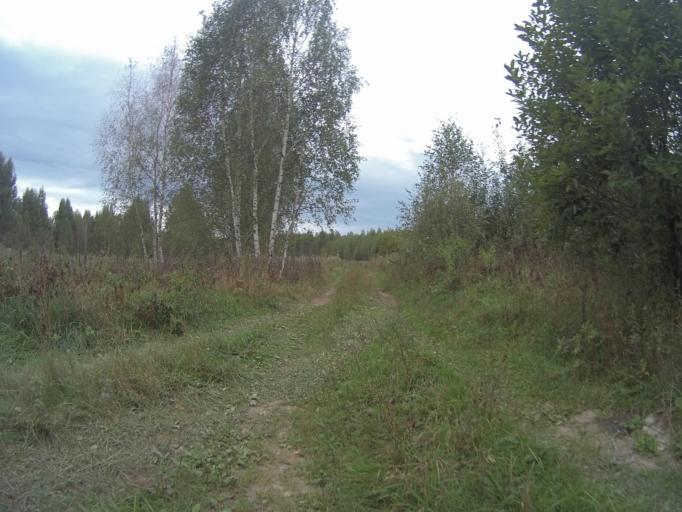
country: RU
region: Vladimir
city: Golovino
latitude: 55.9809
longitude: 40.5080
